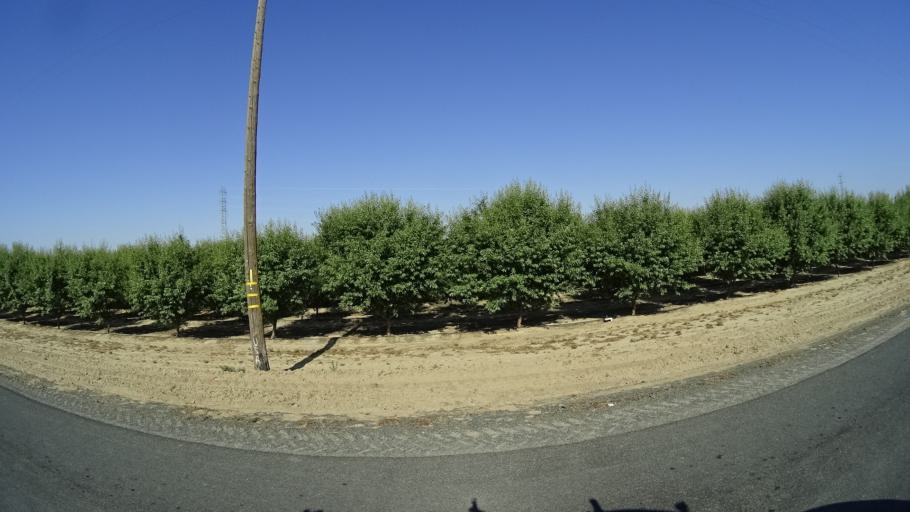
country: US
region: California
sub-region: Fresno County
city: Riverdale
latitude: 36.3674
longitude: -119.8872
